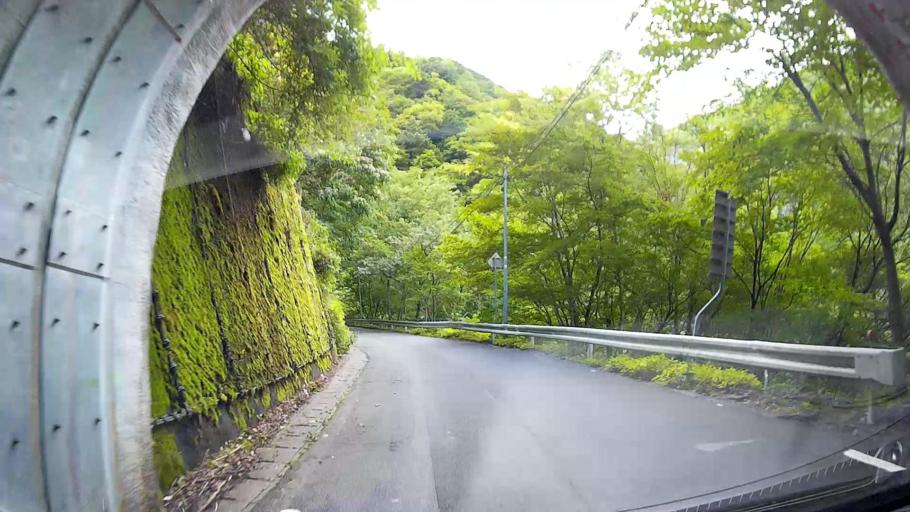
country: JP
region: Shizuoka
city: Shizuoka-shi
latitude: 35.2721
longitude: 138.2207
